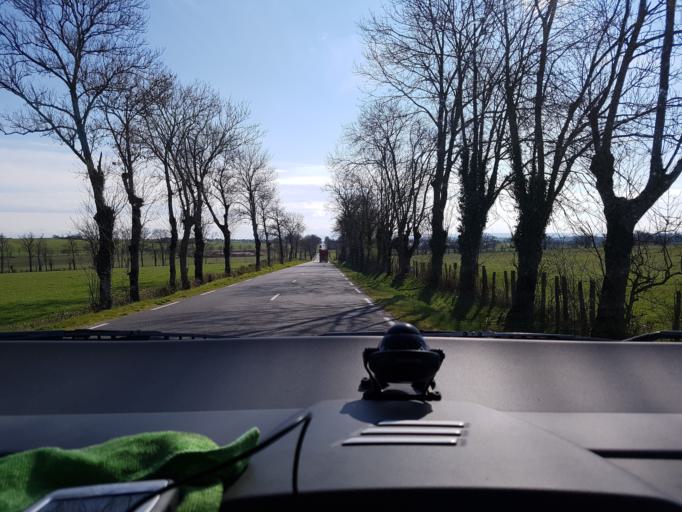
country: FR
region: Midi-Pyrenees
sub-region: Departement de l'Aveyron
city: Druelle
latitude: 44.3696
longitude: 2.4892
